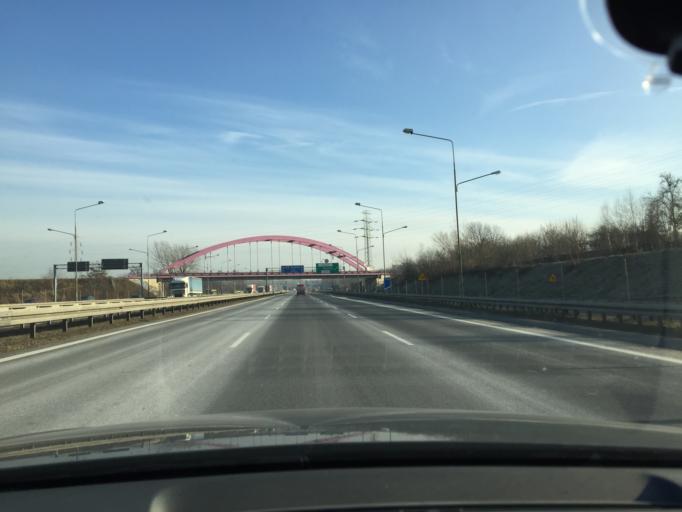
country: PL
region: Silesian Voivodeship
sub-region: Katowice
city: Katowice
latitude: 50.2526
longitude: 18.9861
